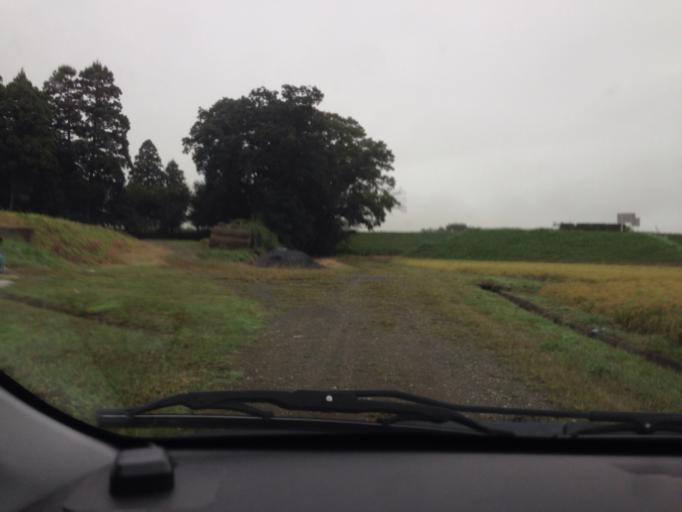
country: JP
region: Fukushima
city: Kitakata
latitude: 37.5895
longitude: 139.8679
